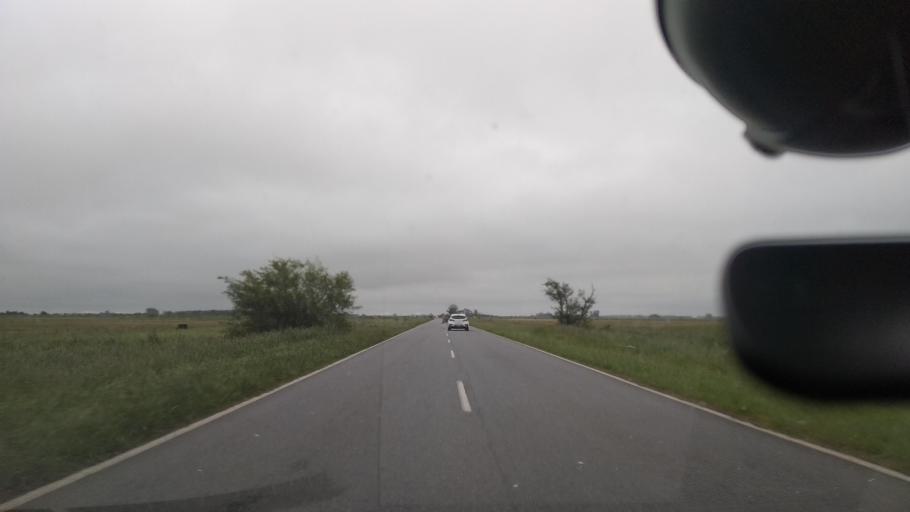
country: AR
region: Buenos Aires
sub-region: Partido de Magdalena
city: Magdalena
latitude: -35.2506
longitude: -57.6684
